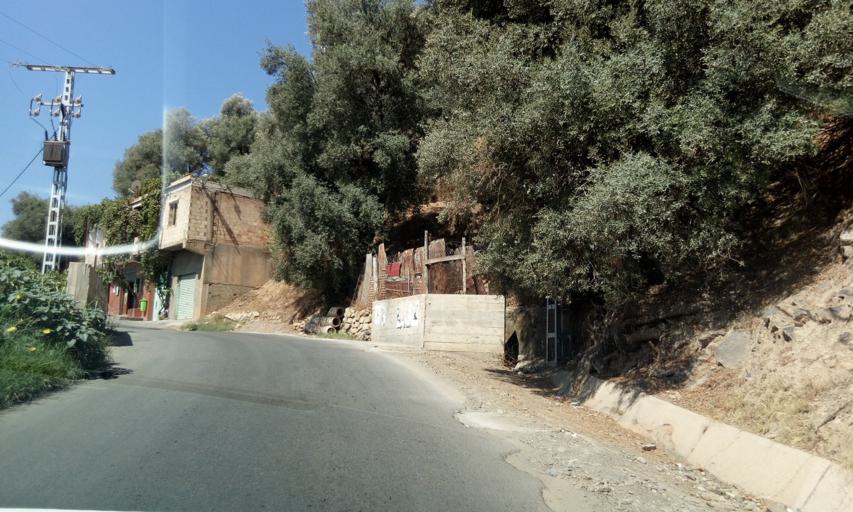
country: DZ
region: Tizi Ouzou
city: Chemini
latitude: 36.6068
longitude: 4.6515
